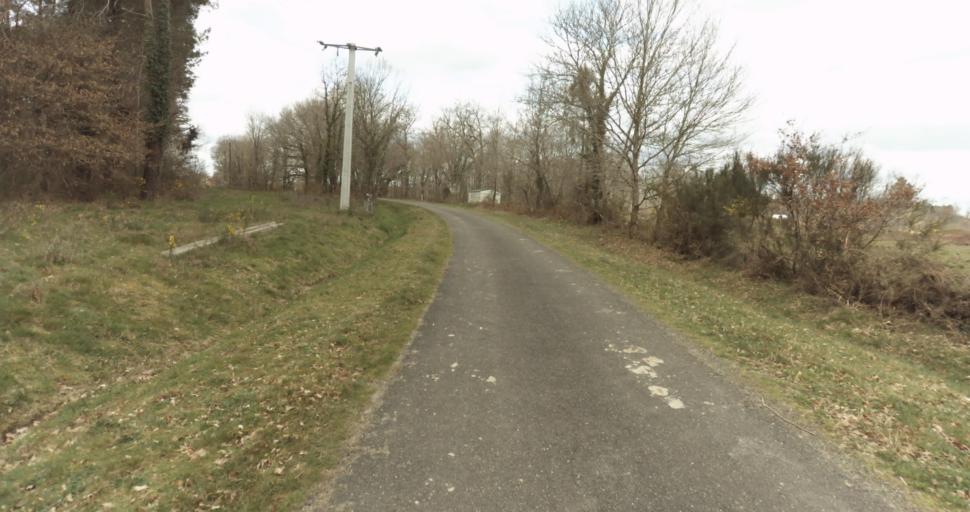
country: FR
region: Aquitaine
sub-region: Departement des Landes
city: Roquefort
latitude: 44.0763
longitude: -0.3984
